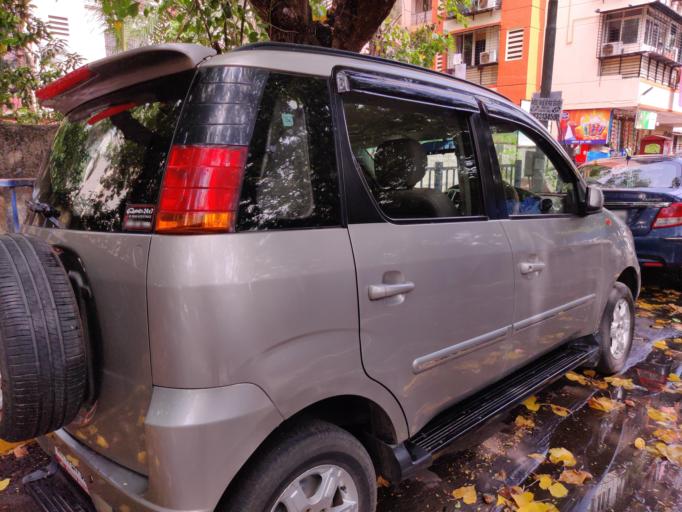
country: IN
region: Maharashtra
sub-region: Mumbai Suburban
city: Borivli
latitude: 19.2575
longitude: 72.8555
